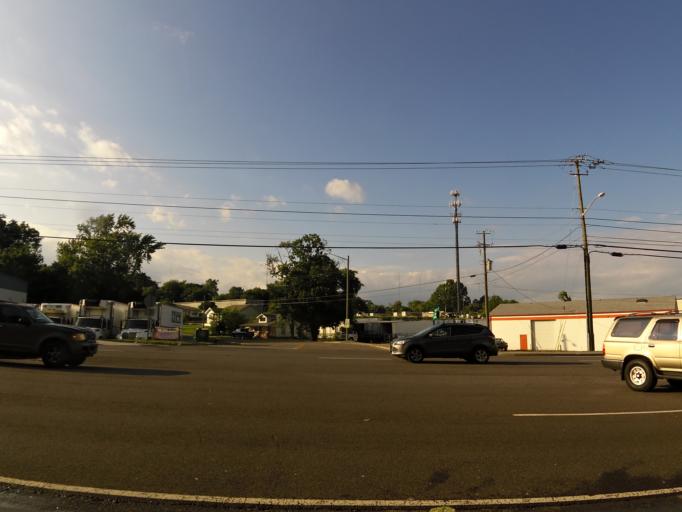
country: US
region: Tennessee
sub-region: Knox County
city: Knoxville
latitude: 35.9638
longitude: -83.9563
